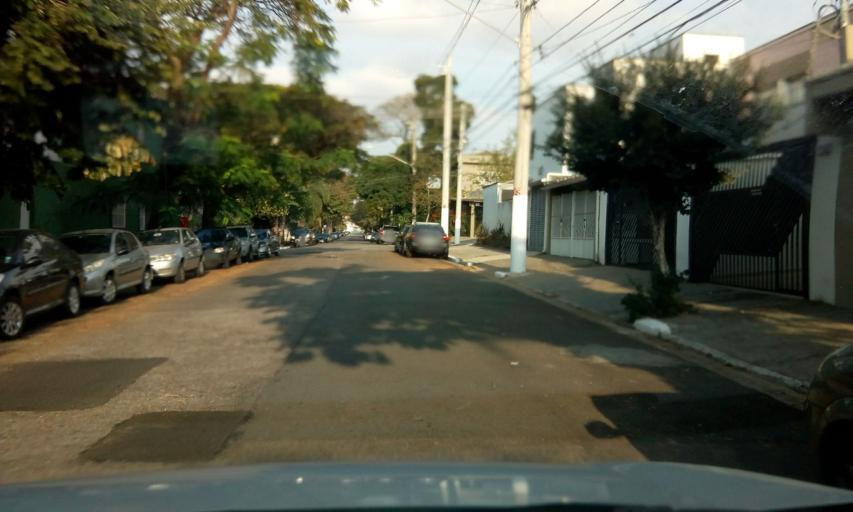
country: BR
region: Sao Paulo
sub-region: Sao Paulo
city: Sao Paulo
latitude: -23.6151
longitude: -46.6541
